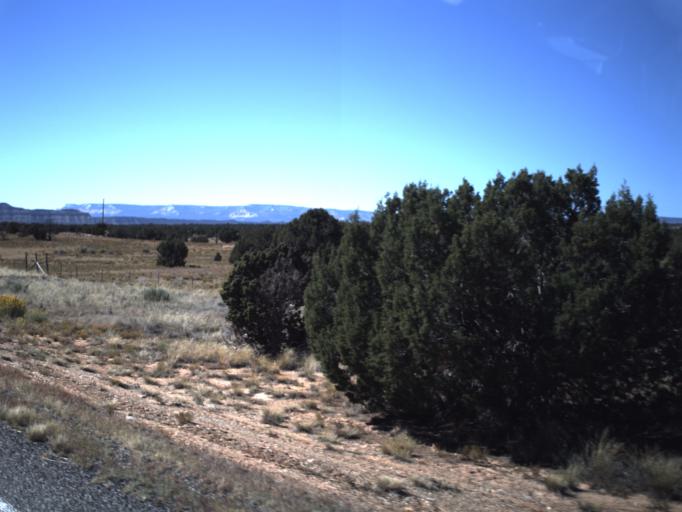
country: US
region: Utah
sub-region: Wayne County
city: Loa
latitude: 37.7470
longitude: -111.4953
